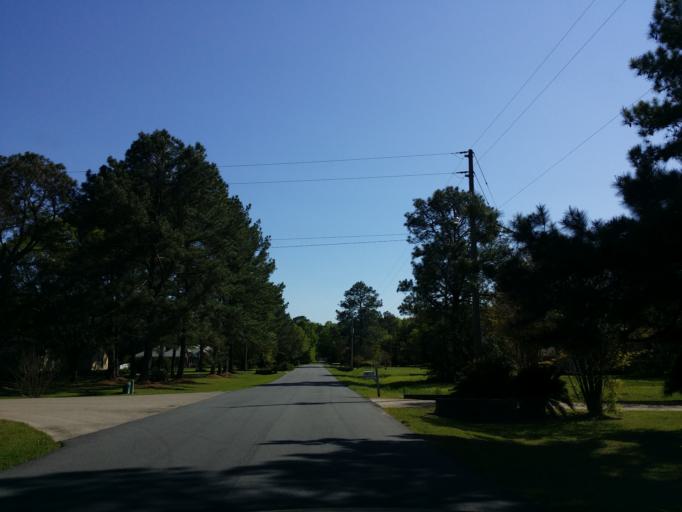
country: US
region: Florida
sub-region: Leon County
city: Tallahassee
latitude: 30.4843
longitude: -84.1903
